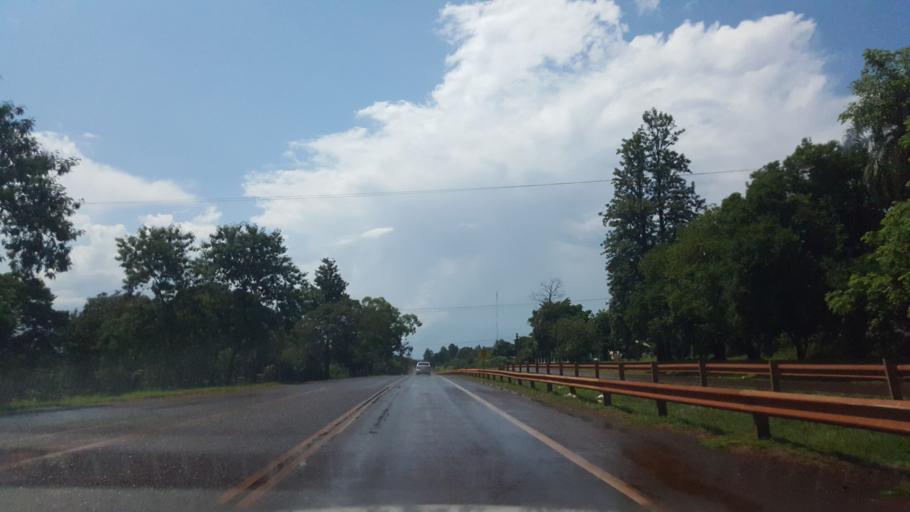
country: AR
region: Misiones
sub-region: Departamento de Eldorado
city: Eldorado
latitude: -26.3988
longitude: -54.6334
